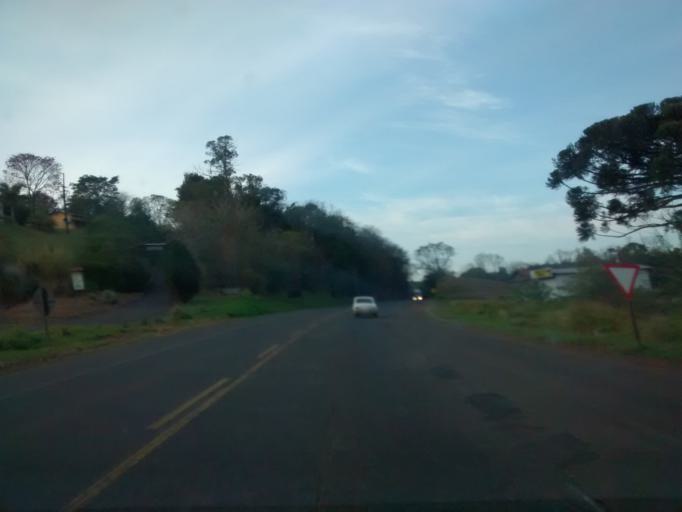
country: BR
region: Parana
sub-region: Francisco Beltrao
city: Francisco Beltrao
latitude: -26.1040
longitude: -53.0580
